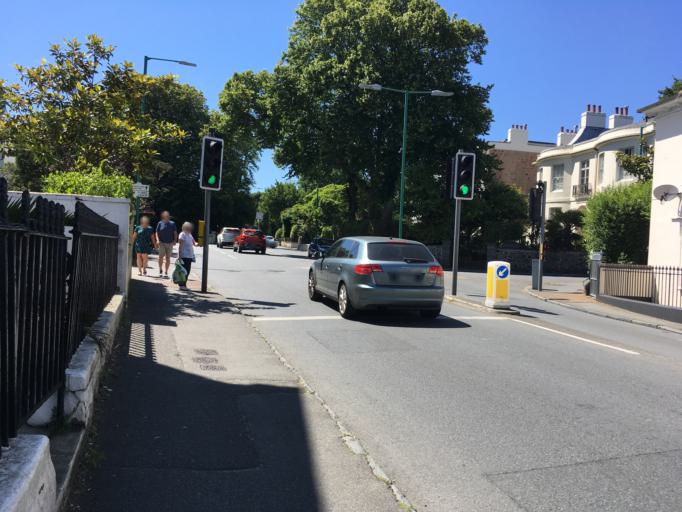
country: GG
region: St Peter Port
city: Saint Peter Port
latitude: 49.4558
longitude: -2.5472
